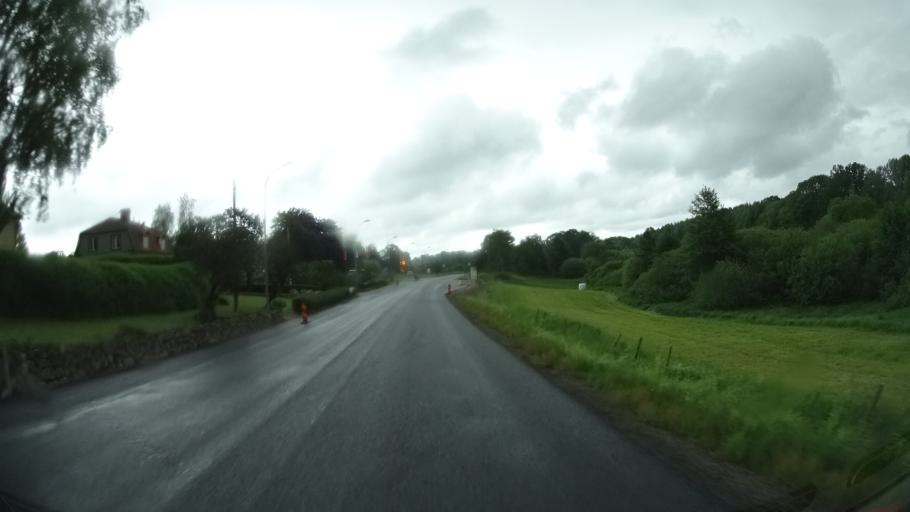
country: SE
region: Kalmar
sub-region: Oskarshamns Kommun
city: Oskarshamn
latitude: 57.3966
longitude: 16.2061
